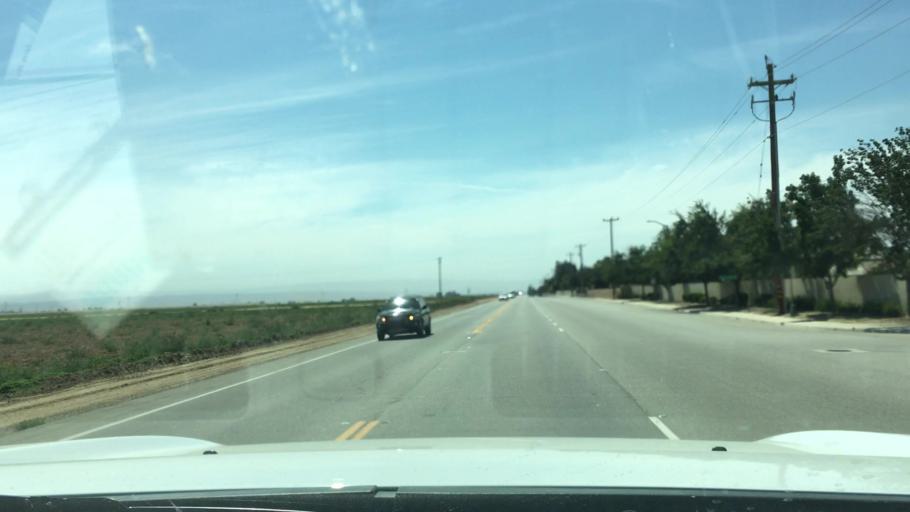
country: US
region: California
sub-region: Kern County
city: Rosedale
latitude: 35.3544
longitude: -119.1873
